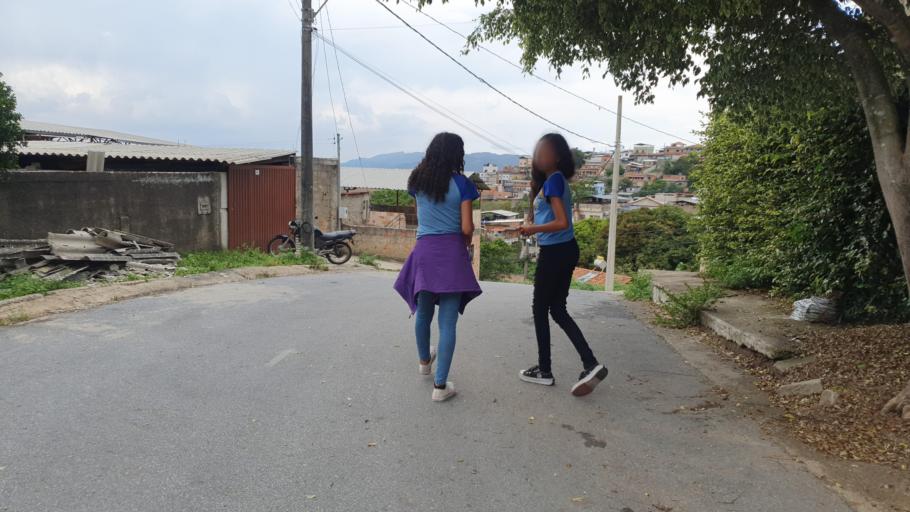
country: BR
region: Minas Gerais
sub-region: Sao Joao Del Rei
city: Sao Joao del Rei
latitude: -21.1261
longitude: -44.2653
